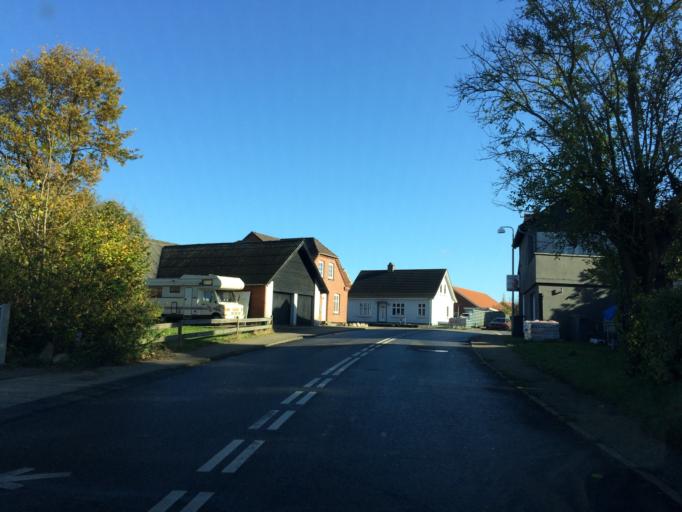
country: DK
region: South Denmark
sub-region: Fredericia Kommune
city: Taulov
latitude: 55.5454
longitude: 9.6135
